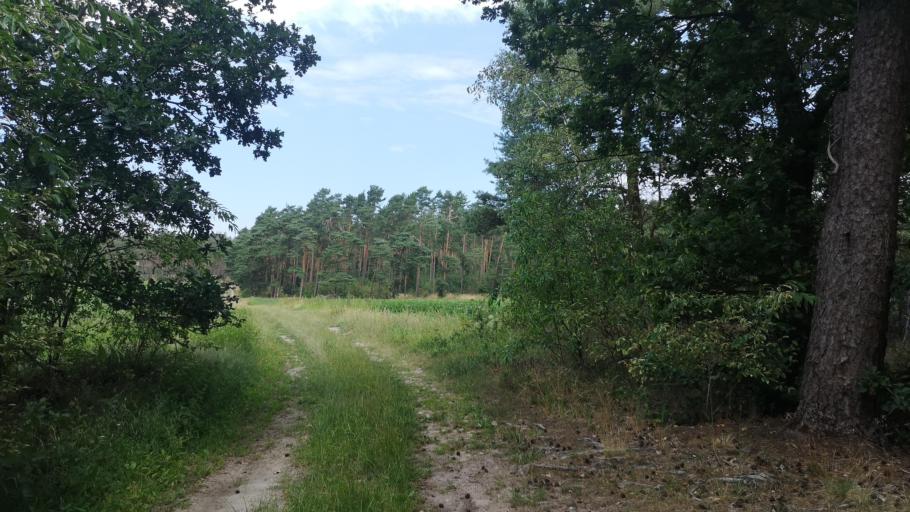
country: DE
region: Lower Saxony
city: Dahlem
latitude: 53.2215
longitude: 10.7328
